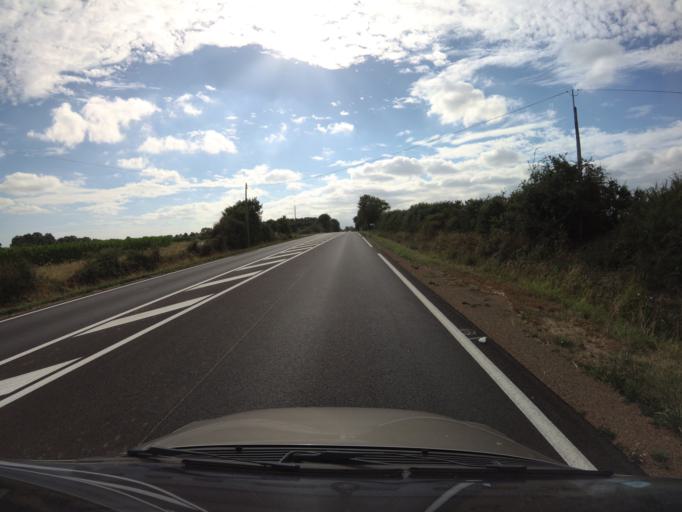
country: FR
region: Pays de la Loire
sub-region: Departement de Maine-et-Loire
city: Vihiers
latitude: 47.1492
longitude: -0.4953
